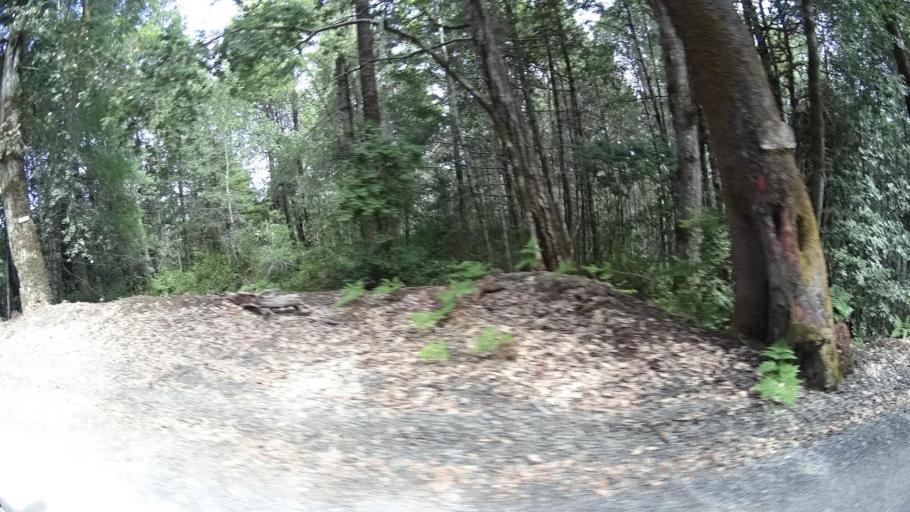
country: US
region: California
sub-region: Humboldt County
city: Redway
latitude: 40.0436
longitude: -123.8472
